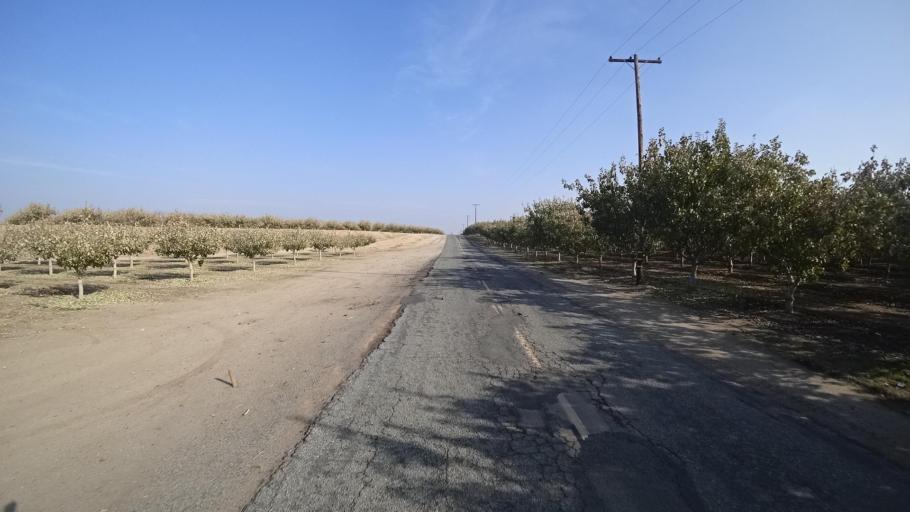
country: US
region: California
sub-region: Tulare County
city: Richgrove
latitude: 35.7908
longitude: -119.1081
